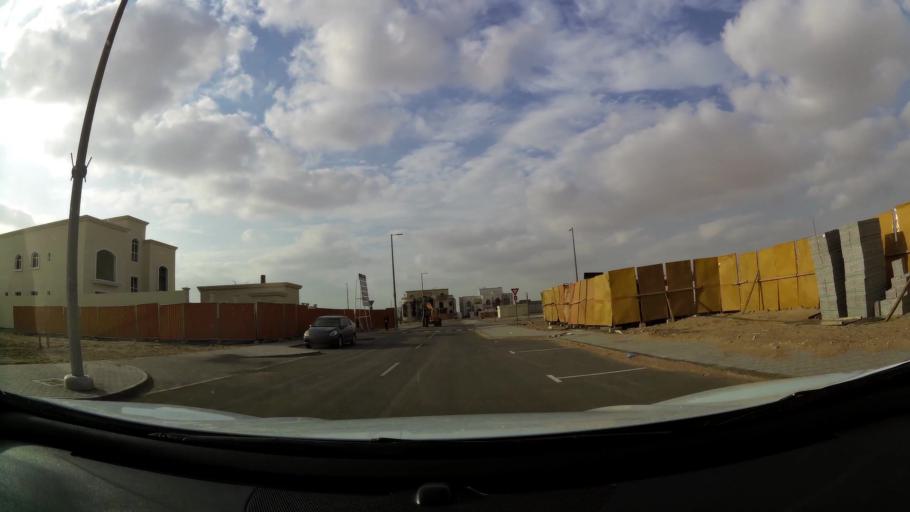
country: AE
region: Abu Dhabi
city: Abu Dhabi
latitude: 24.3404
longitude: 54.5709
